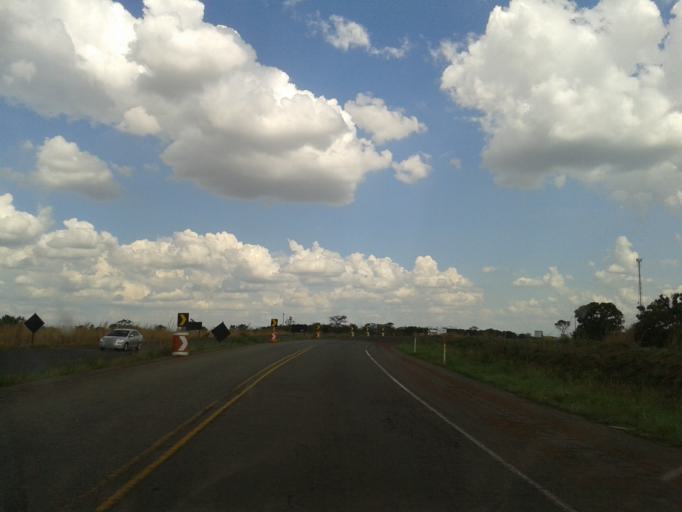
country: BR
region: Goias
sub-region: Caldas Novas
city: Caldas Novas
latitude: -17.6980
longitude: -48.7105
